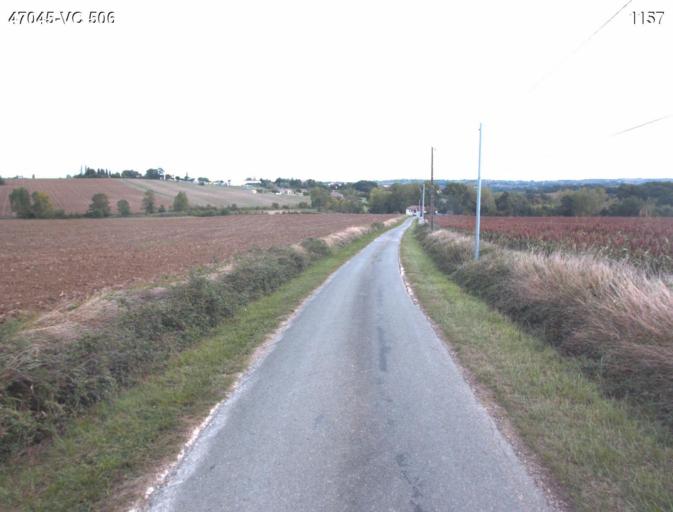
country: FR
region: Aquitaine
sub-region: Departement du Lot-et-Garonne
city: Nerac
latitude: 44.1251
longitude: 0.4066
